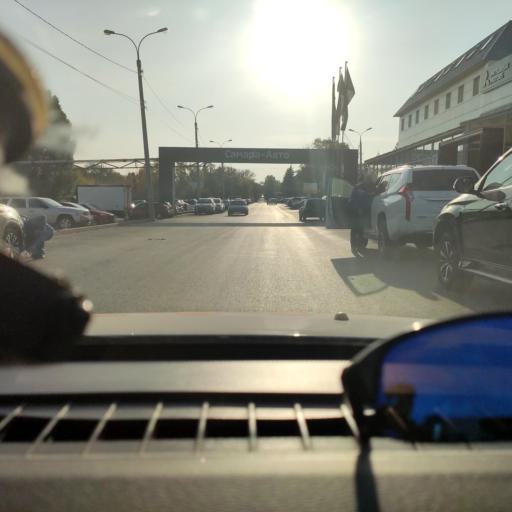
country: RU
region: Samara
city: Samara
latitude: 53.2394
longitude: 50.2489
